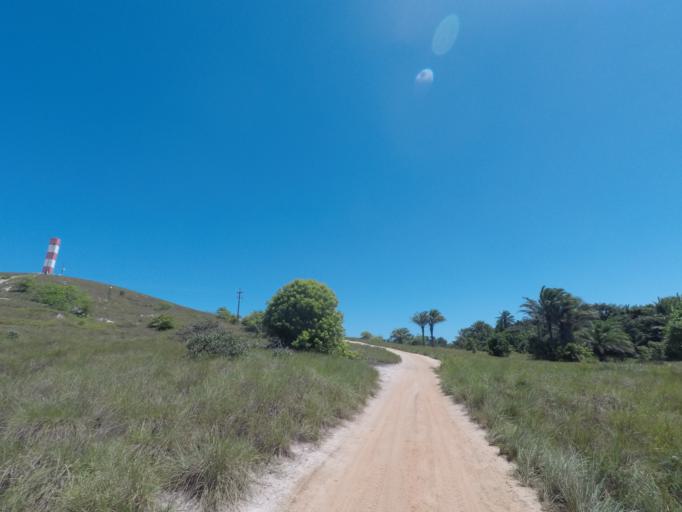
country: BR
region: Bahia
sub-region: Camamu
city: Camamu
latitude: -13.9554
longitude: -38.9451
